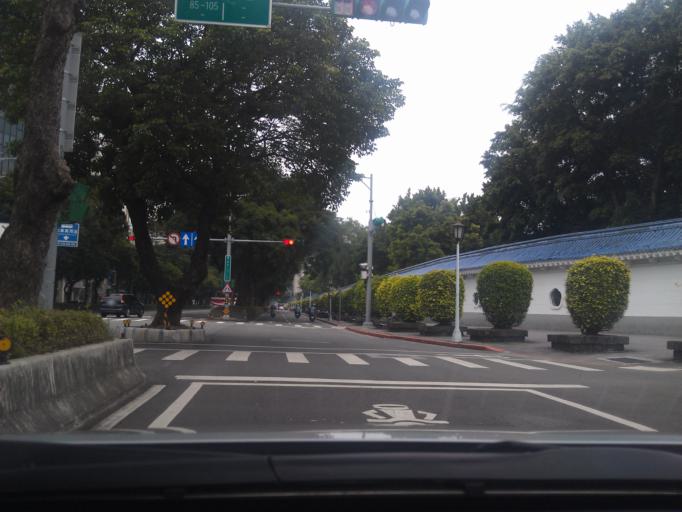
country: TW
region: Taipei
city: Taipei
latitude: 25.0371
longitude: 121.5208
